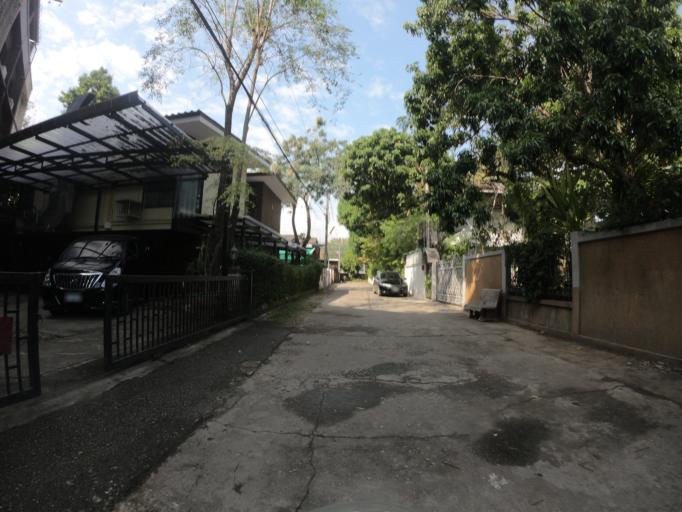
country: TH
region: Chiang Mai
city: Chiang Mai
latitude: 18.8008
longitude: 98.9972
